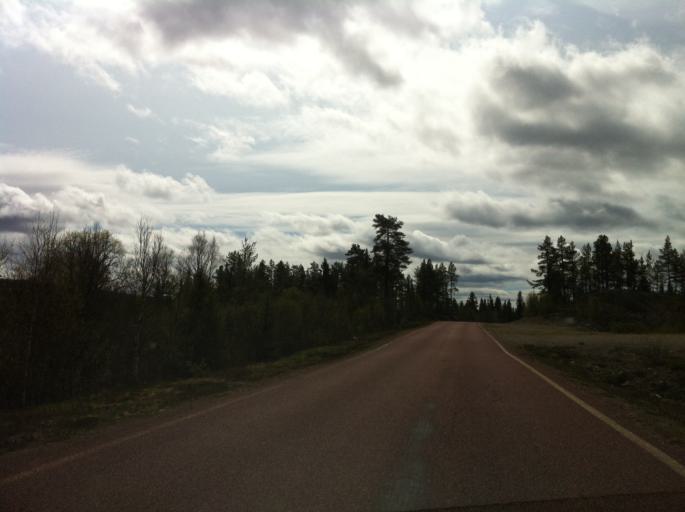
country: NO
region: Hedmark
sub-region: Engerdal
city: Engerdal
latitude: 62.1615
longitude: 12.9429
